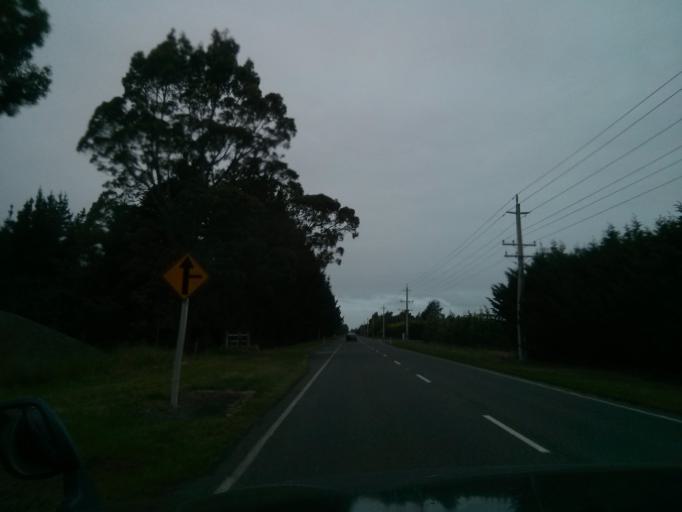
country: NZ
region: Canterbury
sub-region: Waimakariri District
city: Kaiapoi
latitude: -43.3752
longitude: 172.5192
